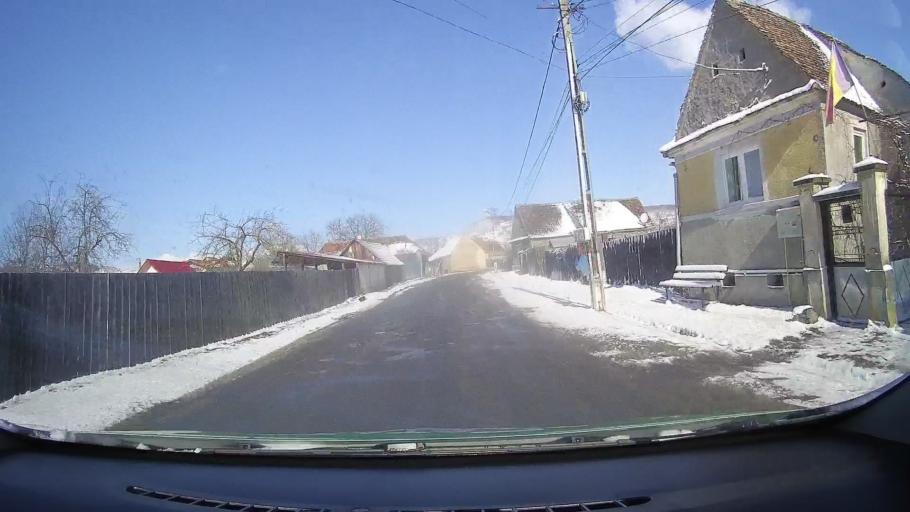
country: RO
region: Sibiu
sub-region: Comuna Avrig
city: Avrig
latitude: 45.7557
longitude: 24.3914
